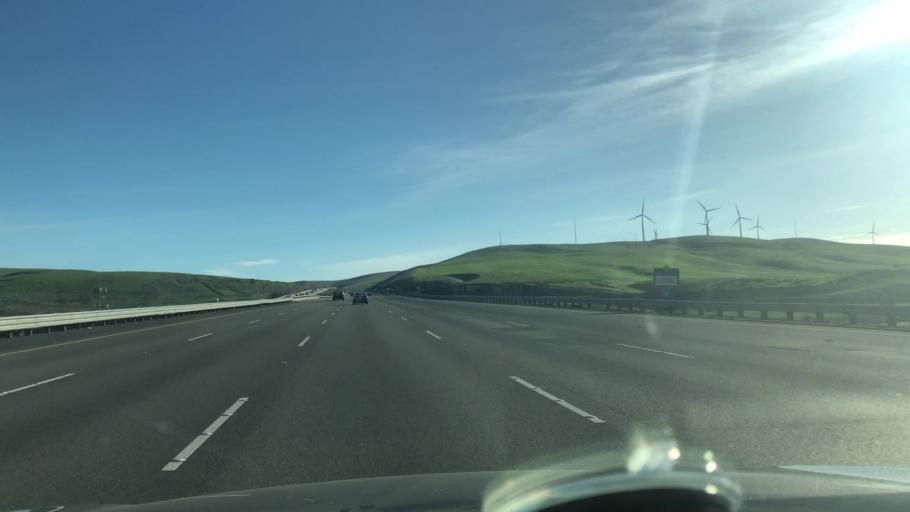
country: US
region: California
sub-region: Alameda County
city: Livermore
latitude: 37.7172
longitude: -121.7030
